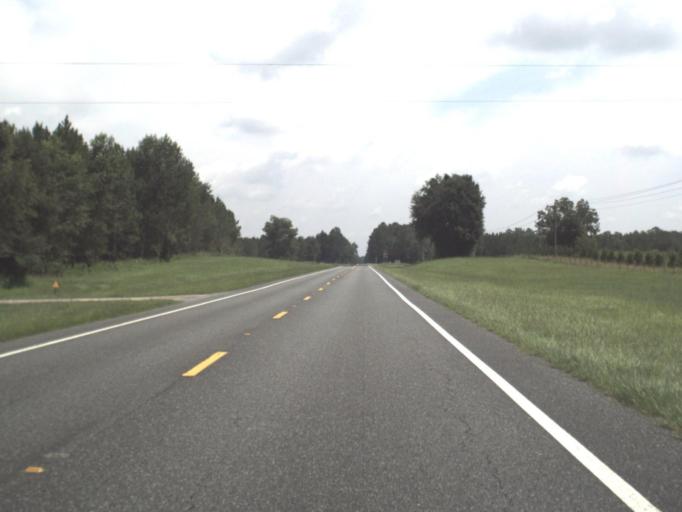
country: US
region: Florida
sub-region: Alachua County
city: High Springs
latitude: 29.9117
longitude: -82.6095
